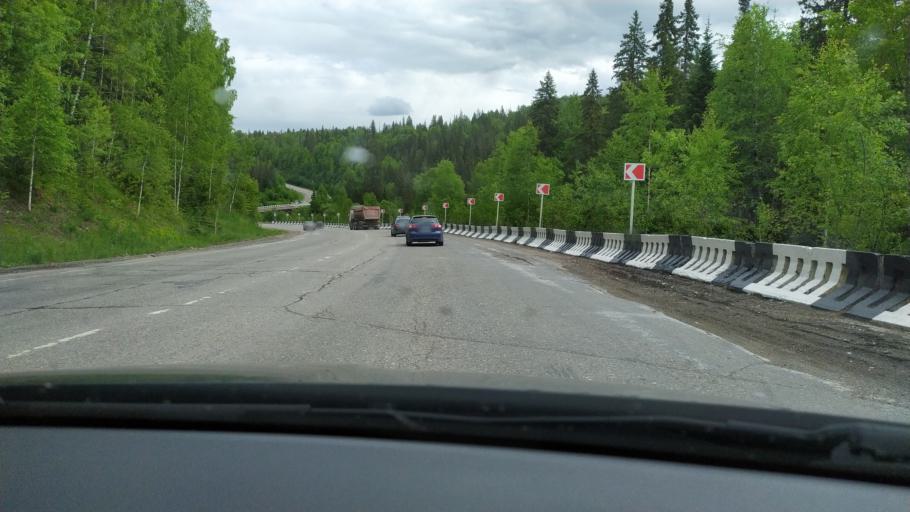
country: RU
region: Perm
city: Gremyachinsk
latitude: 58.4418
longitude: 57.8691
